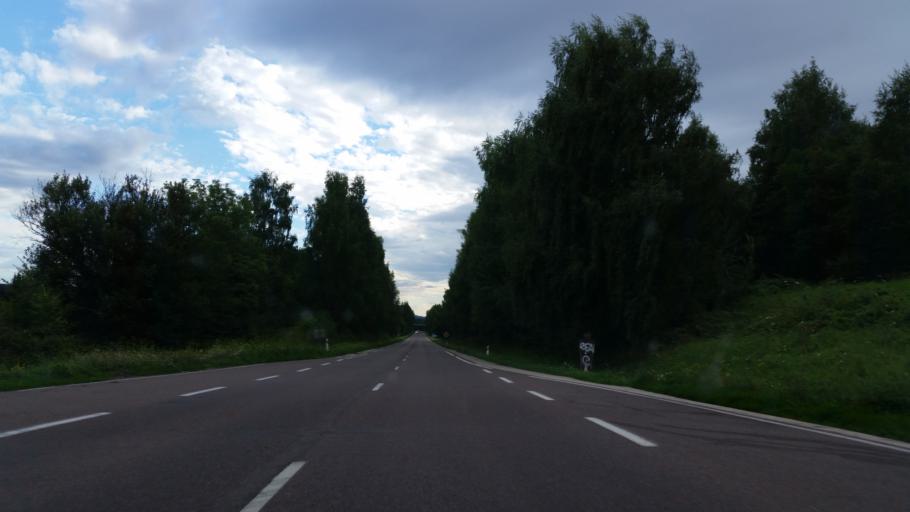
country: FR
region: Franche-Comte
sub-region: Departement de la Haute-Saone
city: Fougerolles
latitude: 47.8993
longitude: 6.4021
